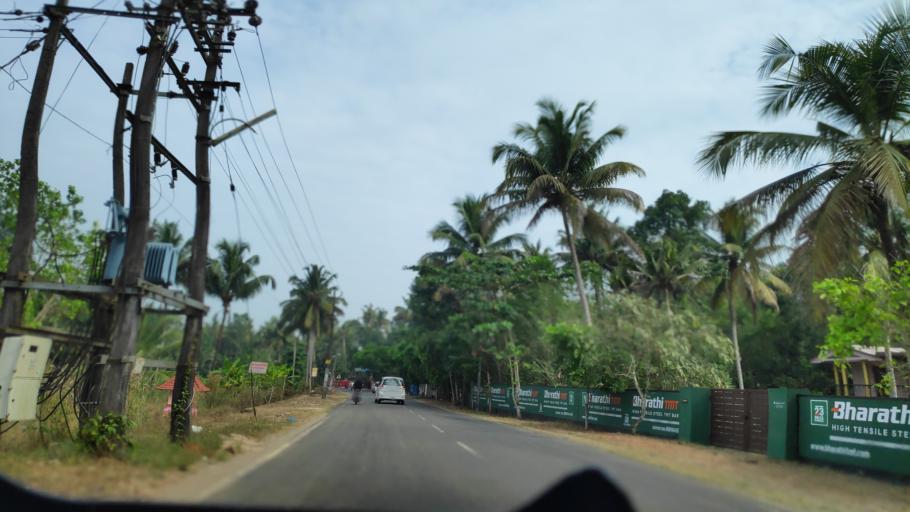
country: IN
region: Kerala
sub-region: Alappuzha
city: Kutiatodu
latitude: 9.7726
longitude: 76.3623
